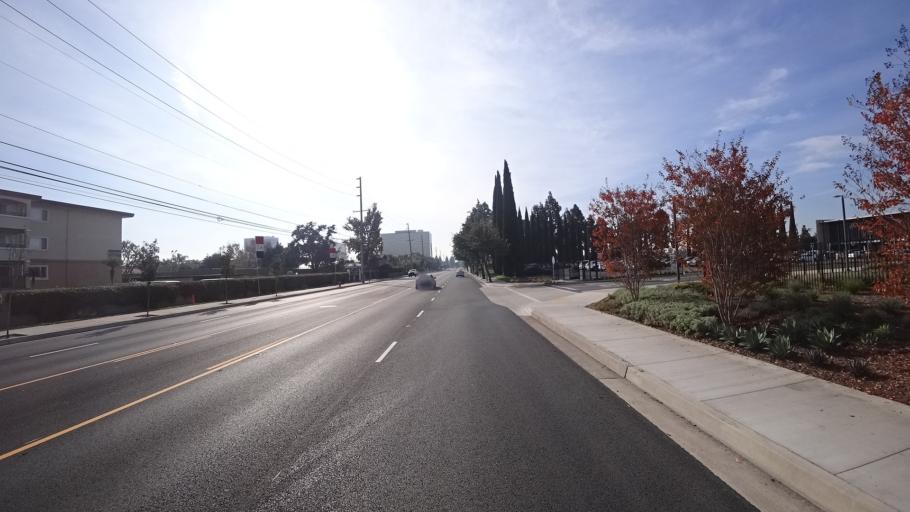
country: US
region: California
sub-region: Orange County
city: Orange
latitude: 33.7871
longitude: -117.8976
